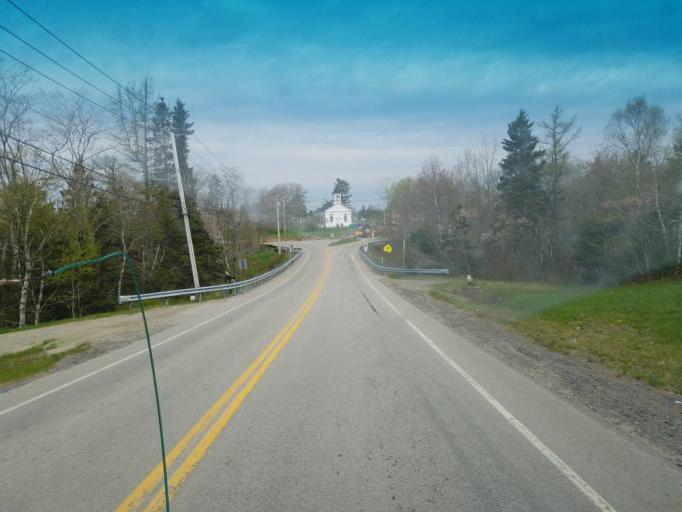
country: US
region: Maine
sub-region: Washington County
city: Eastport
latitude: 44.7895
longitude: -67.1746
